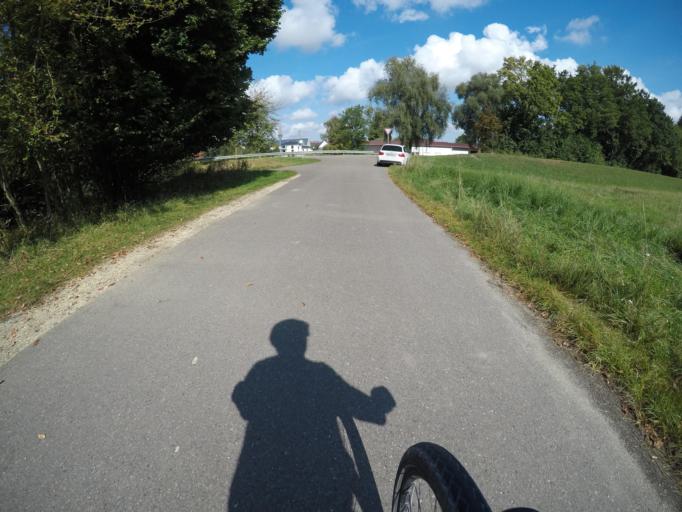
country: DE
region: Bavaria
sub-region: Swabia
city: Schwenningen
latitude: 48.6323
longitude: 10.6495
